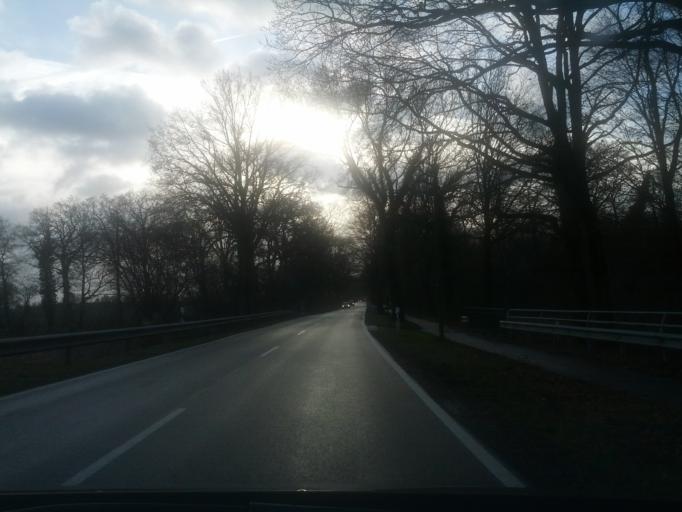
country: DE
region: Lower Saxony
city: Hamersen
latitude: 53.2468
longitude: 9.4836
